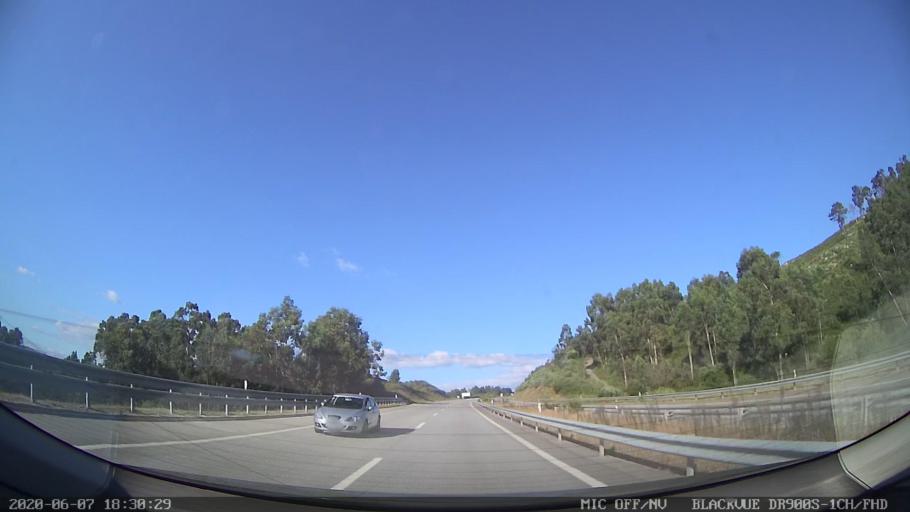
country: PT
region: Braga
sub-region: Fafe
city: Fafe
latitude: 41.4389
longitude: -8.1259
